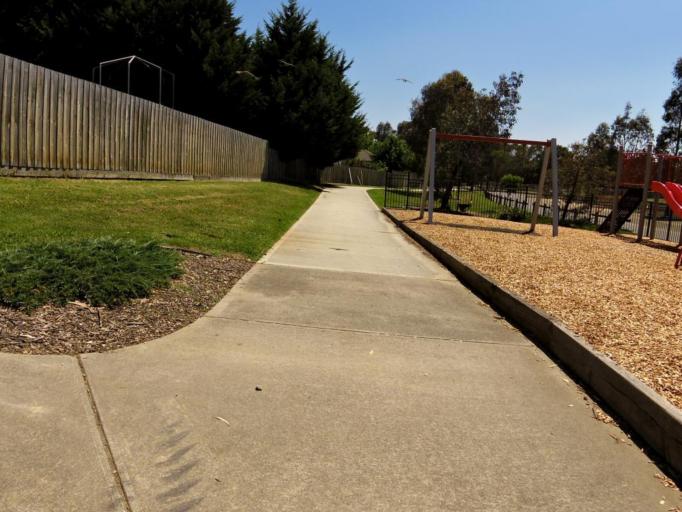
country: AU
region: Victoria
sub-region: Casey
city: Endeavour Hills
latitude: -37.9889
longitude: 145.2736
